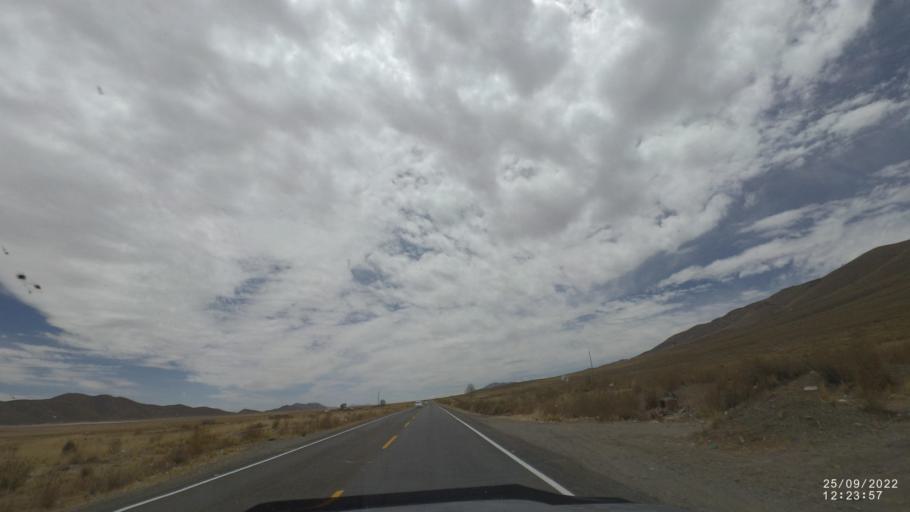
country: BO
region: Oruro
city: Poopo
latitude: -18.3630
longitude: -66.9822
